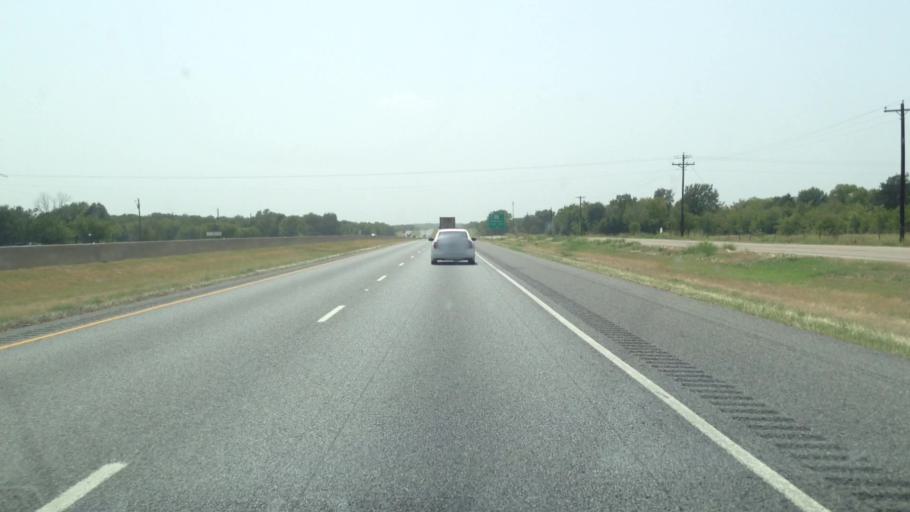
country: US
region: Texas
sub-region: Hunt County
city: Commerce
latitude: 33.1317
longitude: -95.9219
